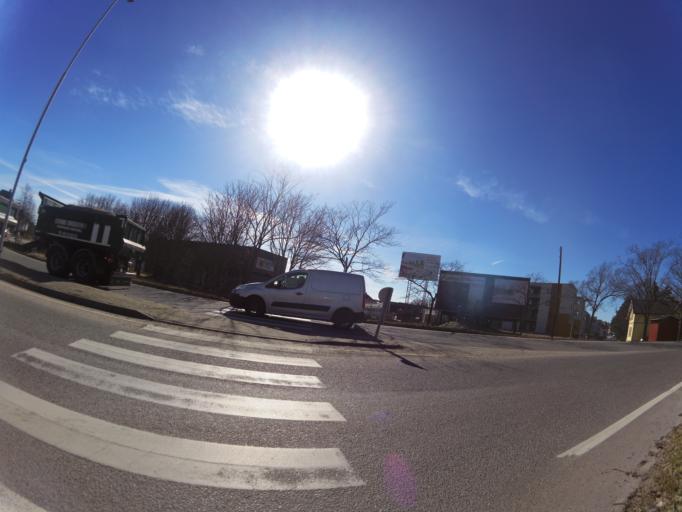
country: NO
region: Ostfold
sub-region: Fredrikstad
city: Fredrikstad
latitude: 59.2199
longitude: 10.9304
